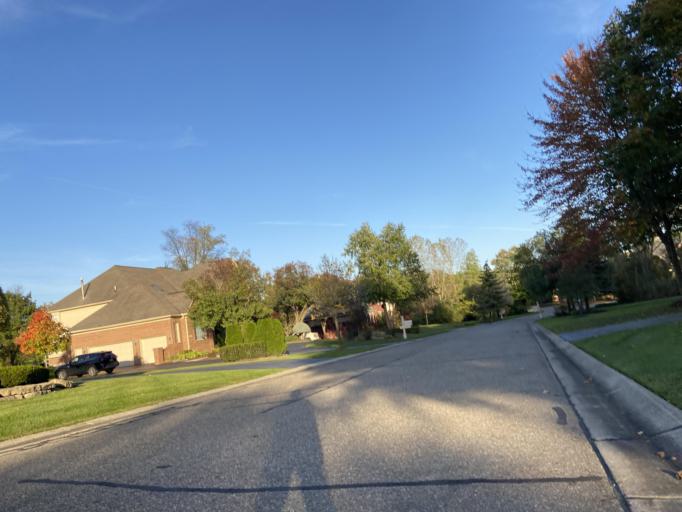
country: US
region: Michigan
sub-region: Oakland County
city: Franklin
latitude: 42.5035
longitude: -83.3378
